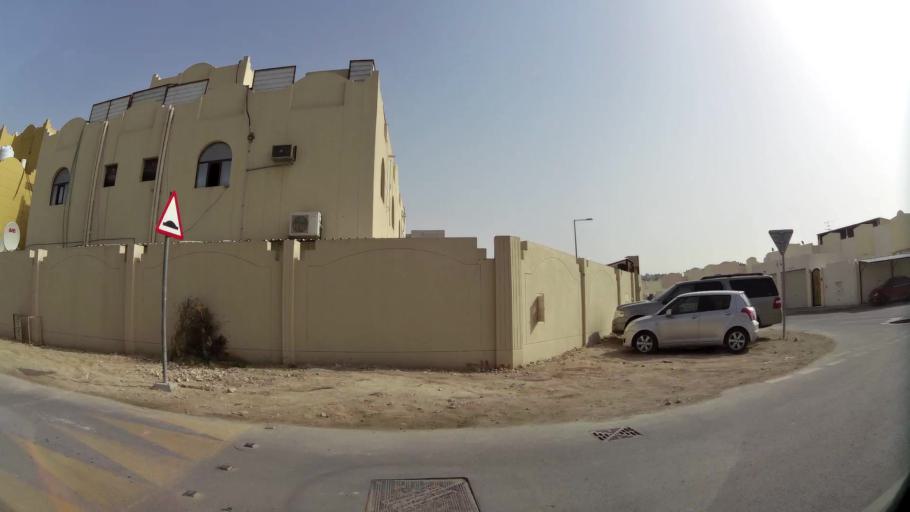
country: QA
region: Baladiyat ar Rayyan
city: Ar Rayyan
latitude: 25.2477
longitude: 51.4400
